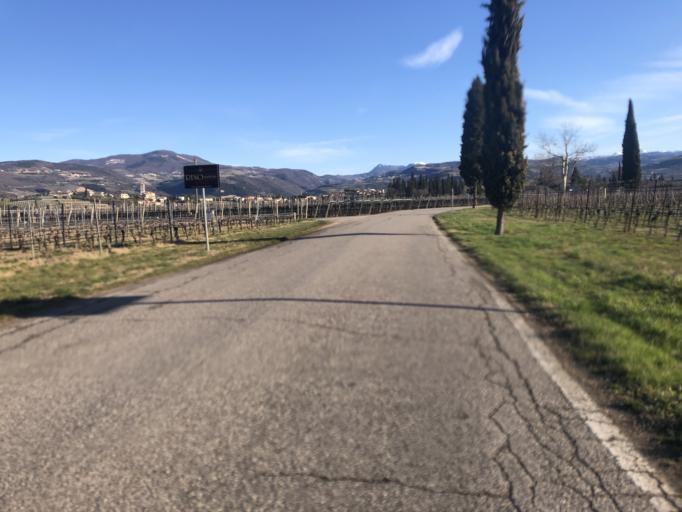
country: IT
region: Veneto
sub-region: Provincia di Verona
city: San Pietro in Cariano
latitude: 45.5025
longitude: 10.8806
